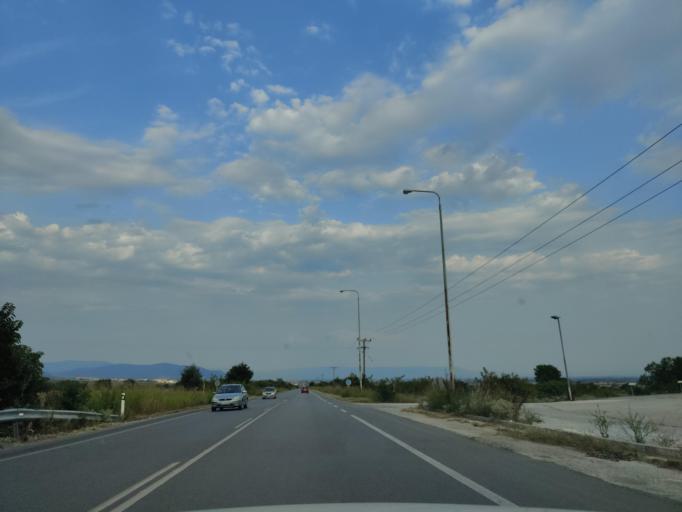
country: GR
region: East Macedonia and Thrace
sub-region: Nomos Dramas
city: Petroussa
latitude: 41.1722
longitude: 24.0278
